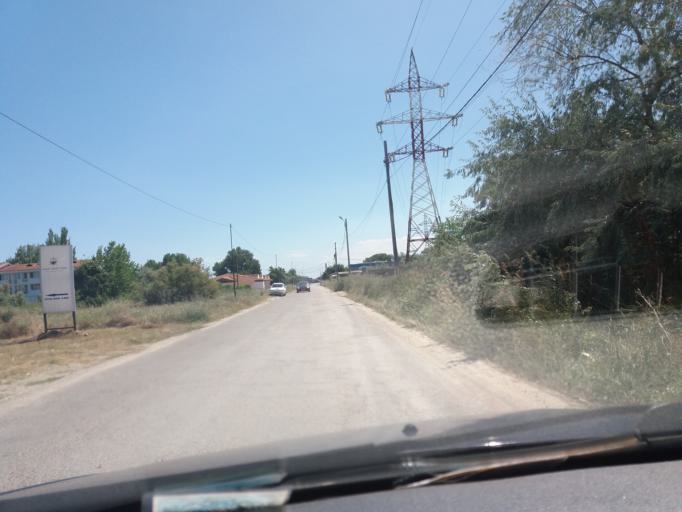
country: RO
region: Constanta
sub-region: Comuna Navodari
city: Navodari
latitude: 44.3216
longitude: 28.6286
